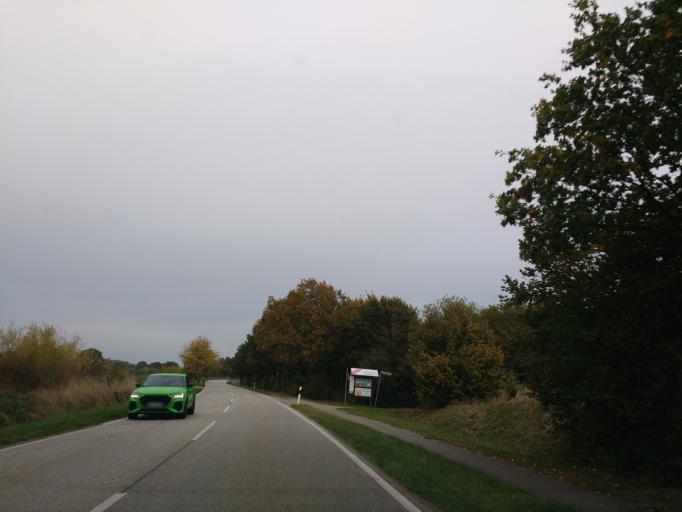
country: DE
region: Schleswig-Holstein
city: Gromitz
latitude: 54.1601
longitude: 10.9641
